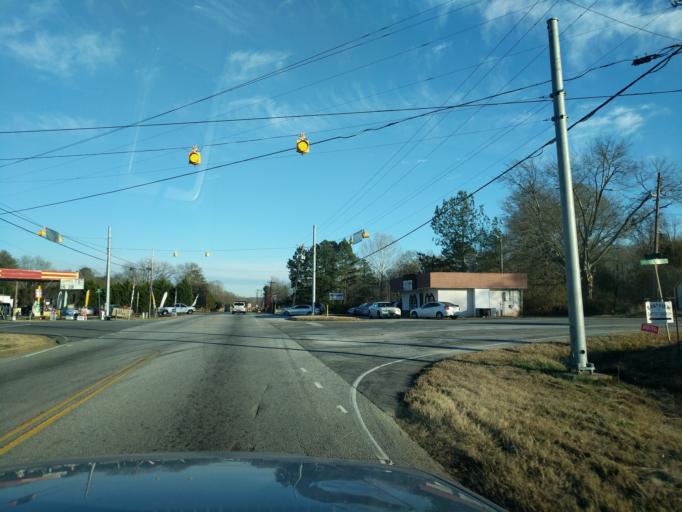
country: US
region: South Carolina
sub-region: Anderson County
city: Williamston
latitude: 34.6406
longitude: -82.4392
